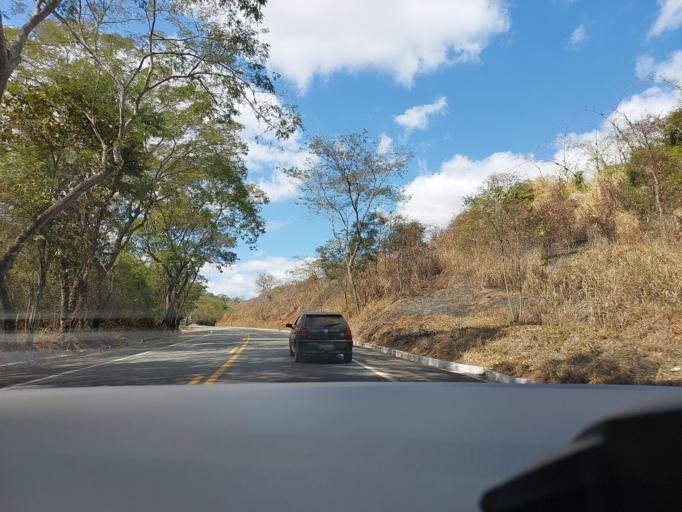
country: BR
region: Minas Gerais
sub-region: Muriae
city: Muriae
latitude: -21.1320
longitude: -42.1918
